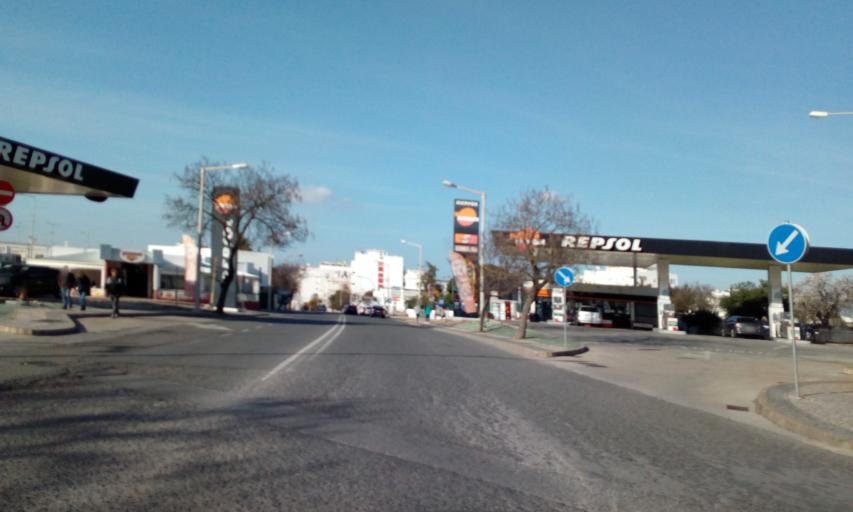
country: PT
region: Faro
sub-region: Faro
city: Faro
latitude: 37.0198
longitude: -7.9232
